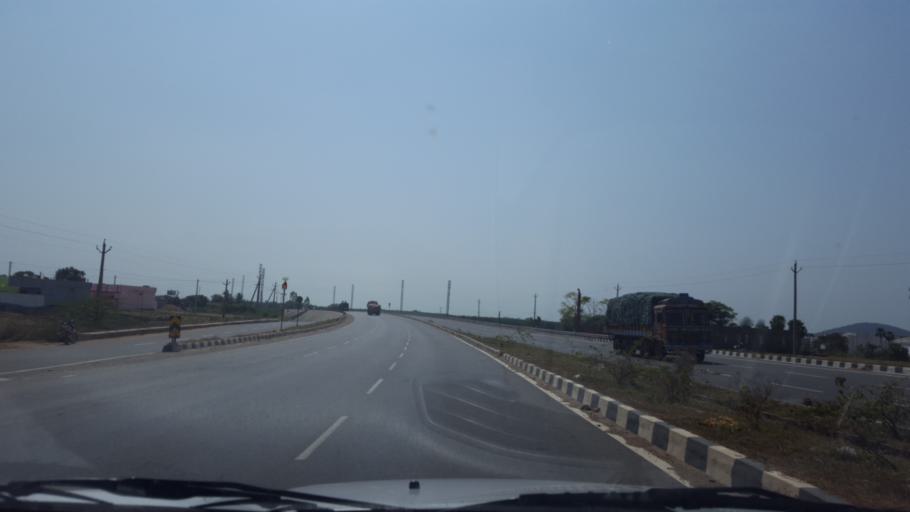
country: IN
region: Andhra Pradesh
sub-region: Prakasam
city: Addanki
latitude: 15.7280
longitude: 80.0088
